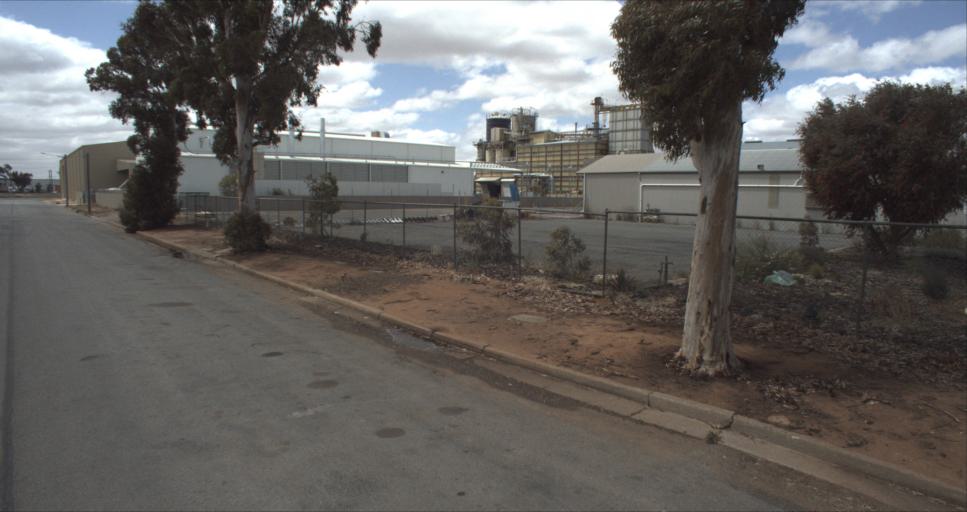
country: AU
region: New South Wales
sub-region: Leeton
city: Leeton
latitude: -34.5556
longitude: 146.3939
